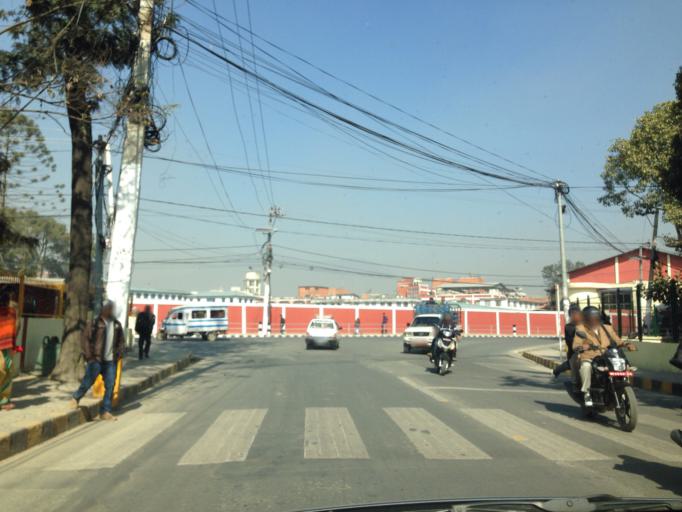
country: NP
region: Central Region
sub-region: Bagmati Zone
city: Kathmandu
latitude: 27.7326
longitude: 85.3291
